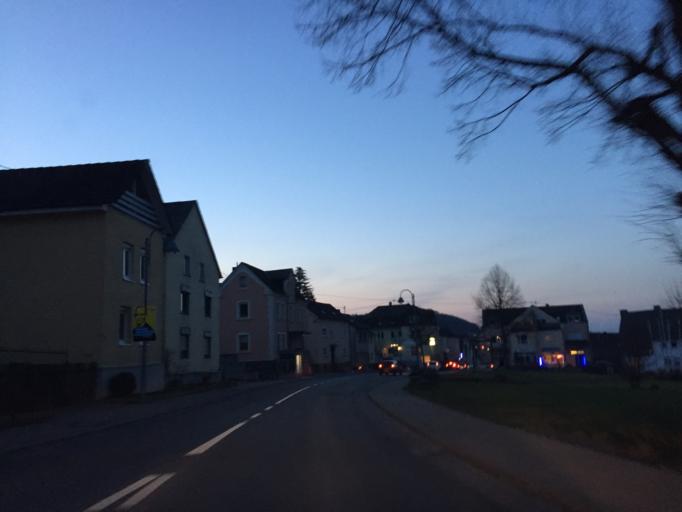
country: DE
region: Rheinland-Pfalz
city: Eppenrod
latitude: 50.4193
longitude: 7.9360
